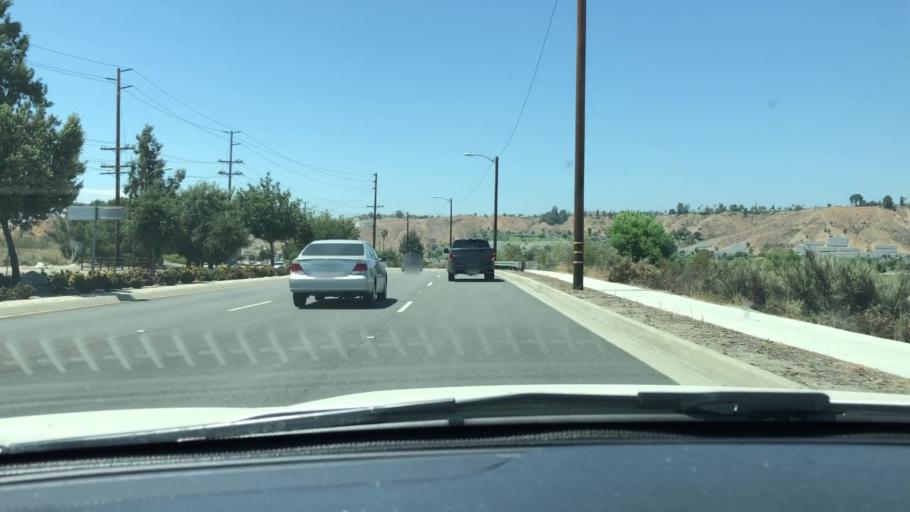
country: US
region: California
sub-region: Los Angeles County
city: Santa Clarita
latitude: 34.4185
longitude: -118.4818
